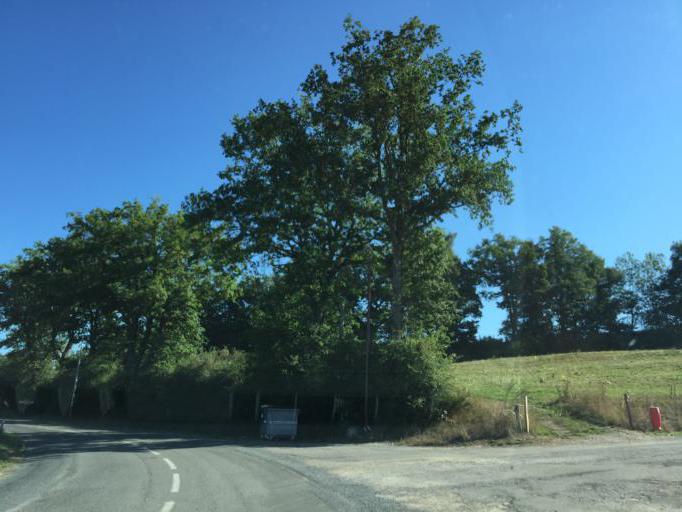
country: FR
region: Midi-Pyrenees
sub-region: Departement de l'Aveyron
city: Pont-de-Salars
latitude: 44.3176
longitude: 2.7538
